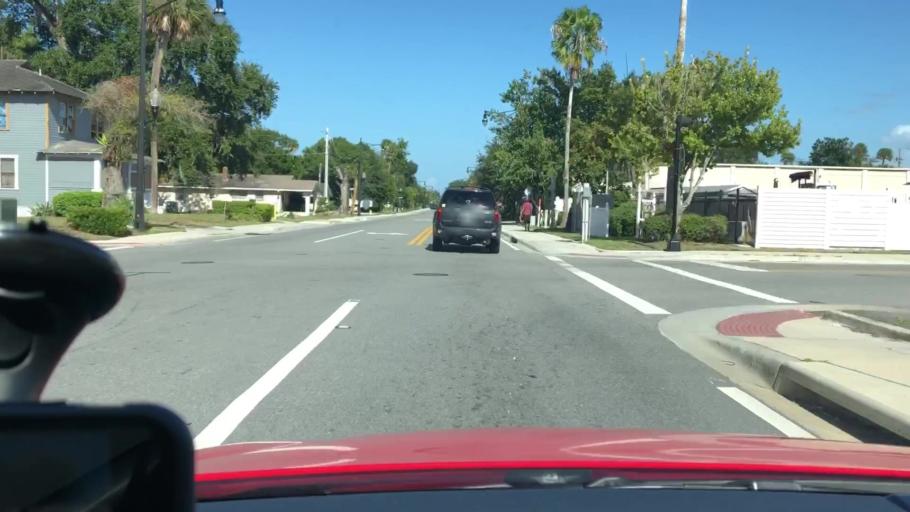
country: US
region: Florida
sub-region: Volusia County
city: Daytona Beach
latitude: 29.2029
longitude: -81.0308
